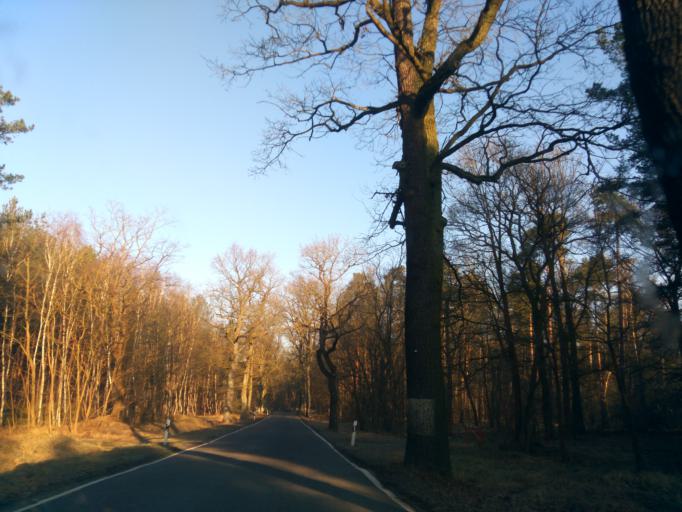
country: DE
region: Brandenburg
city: Falkensee
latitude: 52.6144
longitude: 13.1054
